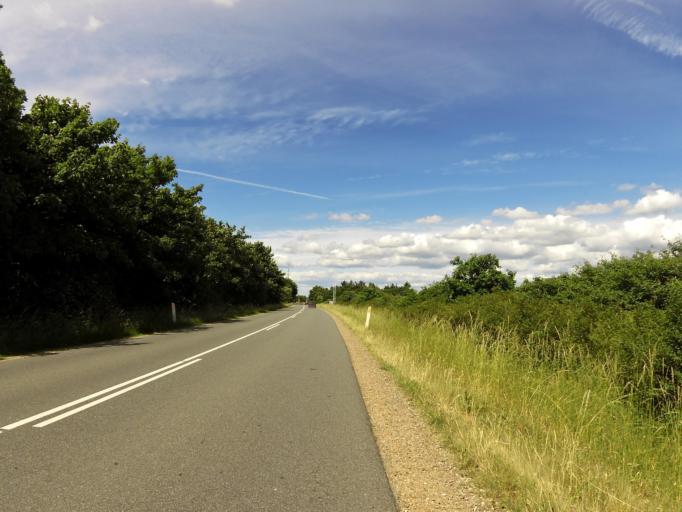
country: DK
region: South Denmark
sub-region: Esbjerg Kommune
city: Ribe
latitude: 55.3084
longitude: 8.7660
